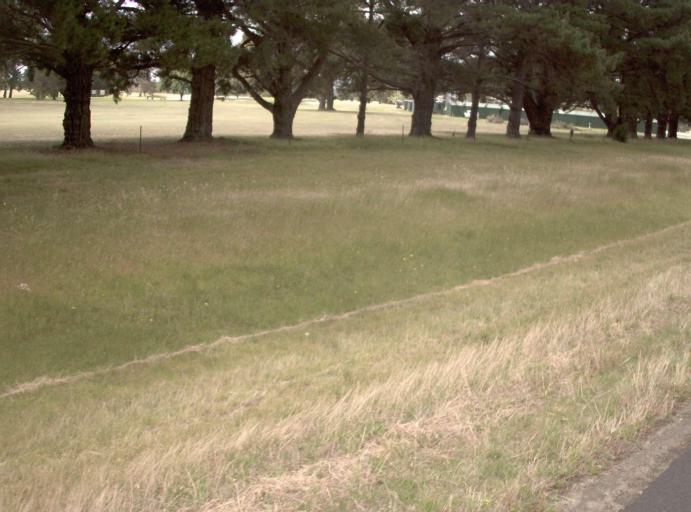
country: AU
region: Victoria
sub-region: Wellington
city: Sale
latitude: -38.1630
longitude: 147.0743
